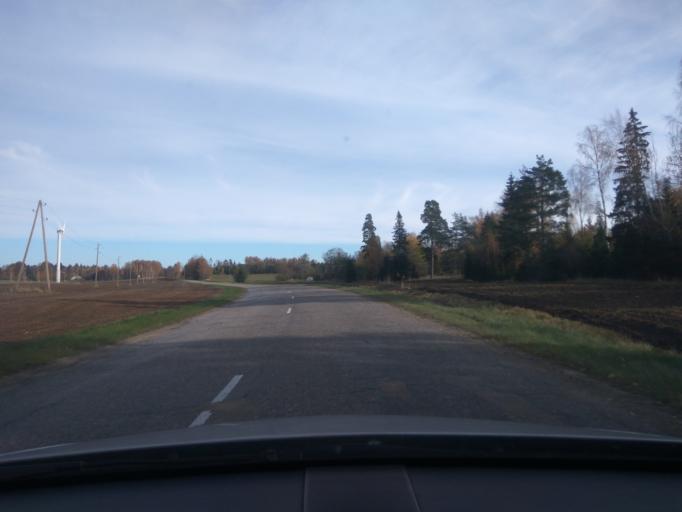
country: LV
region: Alsunga
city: Alsunga
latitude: 56.9898
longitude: 21.6126
